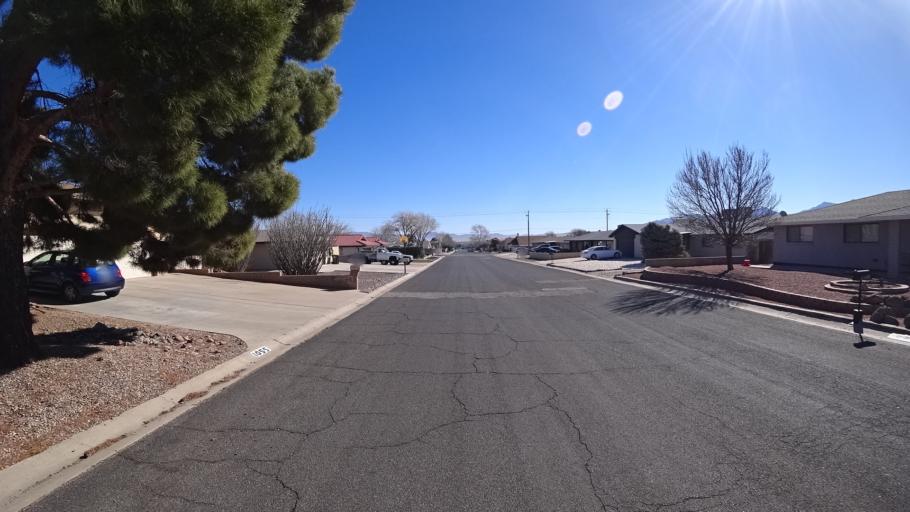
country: US
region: Arizona
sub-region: Mohave County
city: New Kingman-Butler
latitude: 35.2364
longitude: -114.0414
